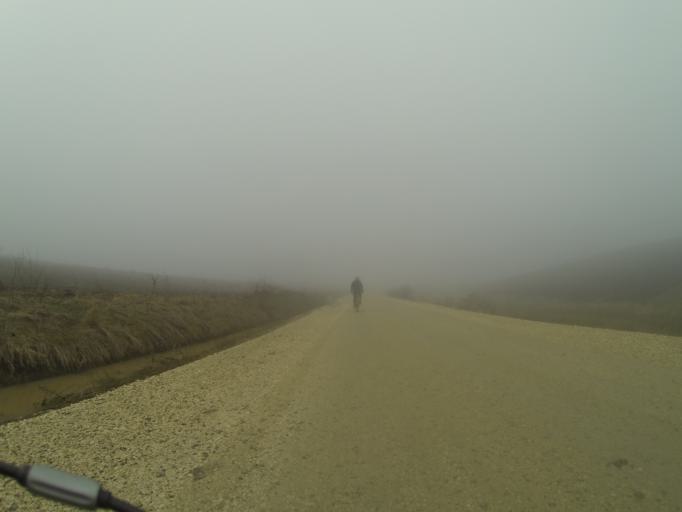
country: RO
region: Mehedinti
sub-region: Comuna Balacita
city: Gvardinita
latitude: 44.4244
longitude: 23.1304
